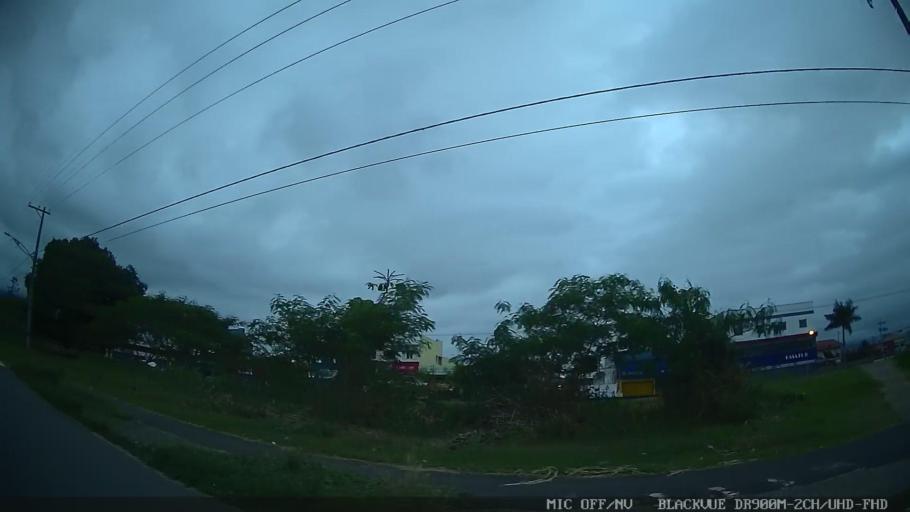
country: BR
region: Sao Paulo
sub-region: Peruibe
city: Peruibe
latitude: -24.3038
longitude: -46.9897
